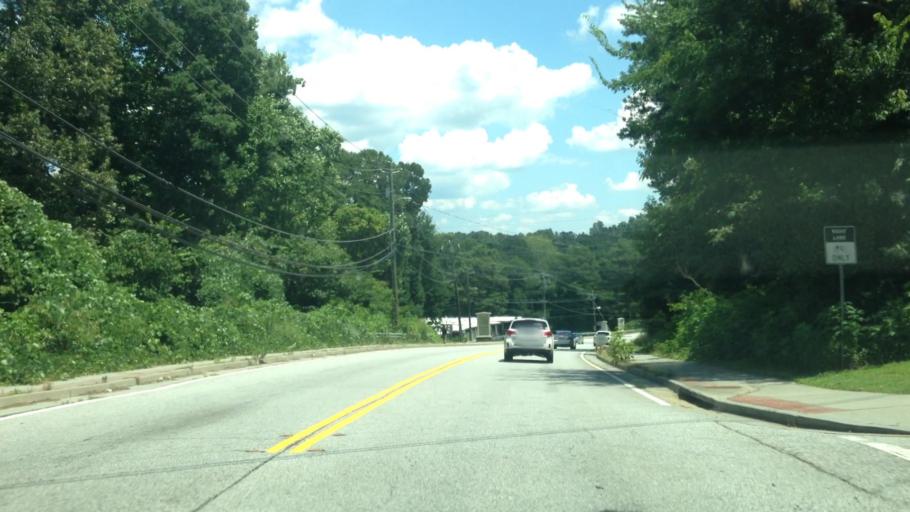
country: US
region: Georgia
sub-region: DeKalb County
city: North Atlanta
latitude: 33.8437
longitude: -84.3242
